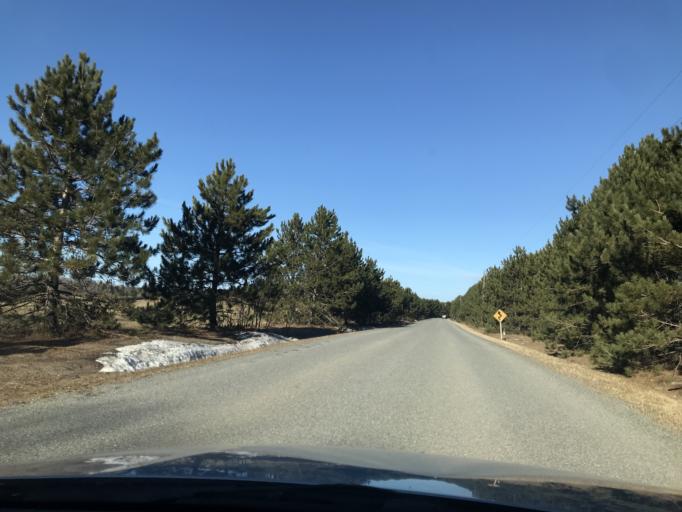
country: US
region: Wisconsin
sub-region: Marinette County
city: Niagara
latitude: 45.3794
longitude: -88.0303
